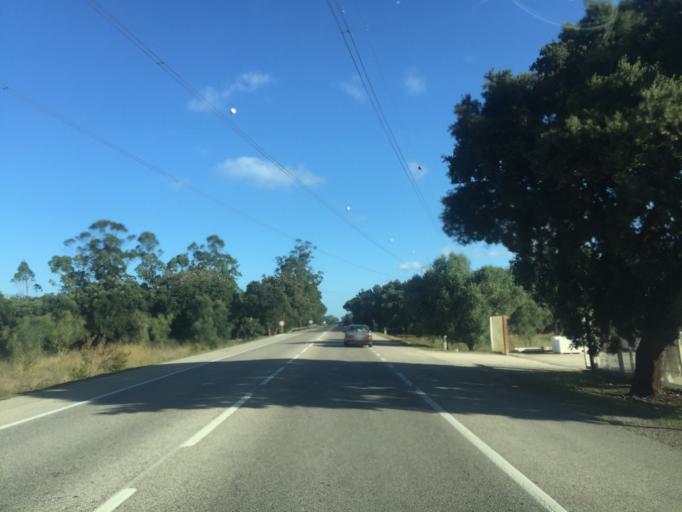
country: PT
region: Leiria
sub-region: Alcobaca
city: Turquel
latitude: 39.4689
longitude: -8.9418
